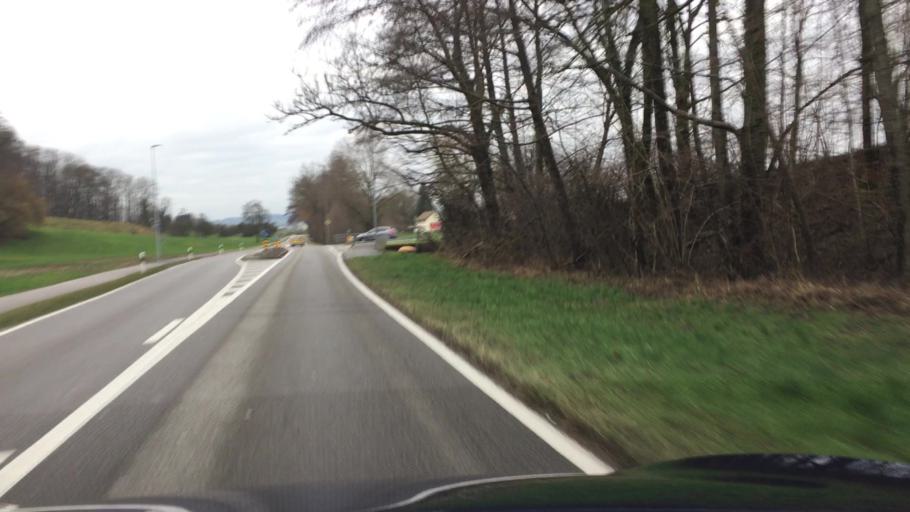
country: CH
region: Thurgau
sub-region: Arbon District
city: Amriswil
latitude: 47.5379
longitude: 9.2978
